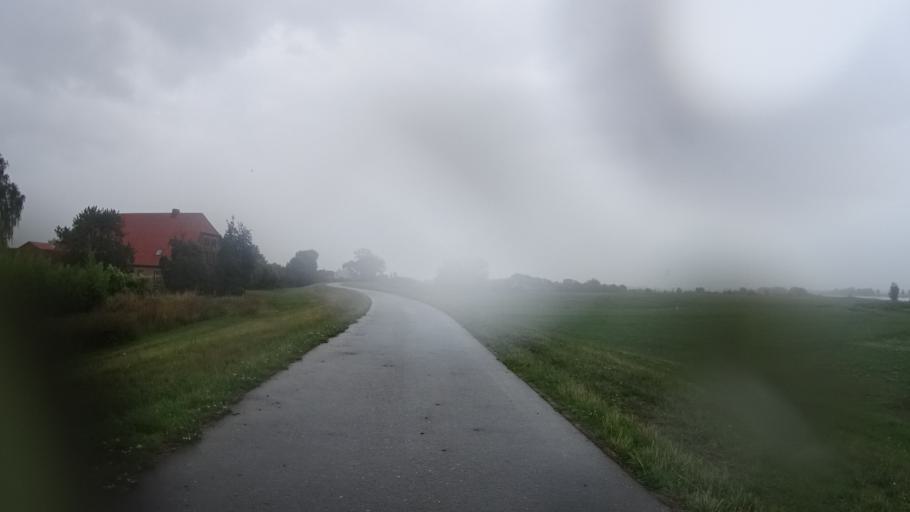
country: DE
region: Lower Saxony
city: Hitzacker
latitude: 53.1656
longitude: 11.0383
